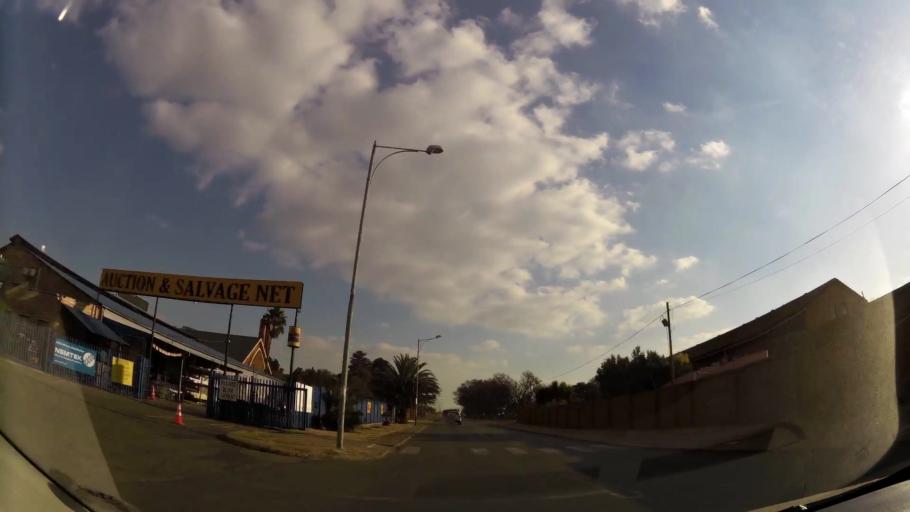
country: ZA
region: Gauteng
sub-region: West Rand District Municipality
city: Krugersdorp
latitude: -26.0988
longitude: 27.7423
